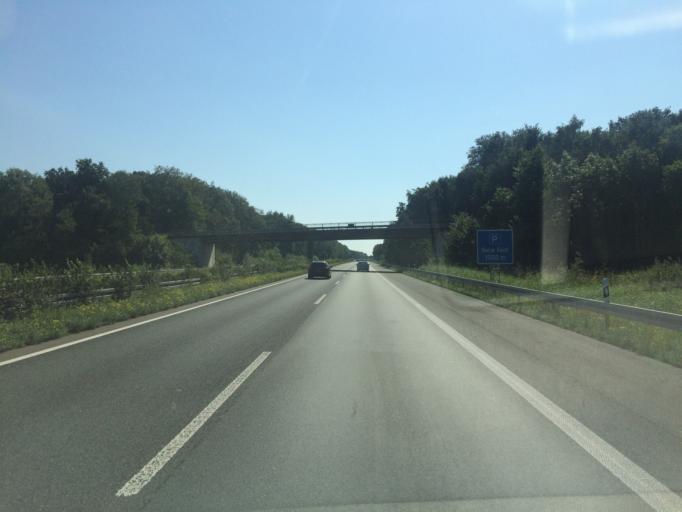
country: DE
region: North Rhine-Westphalia
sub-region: Regierungsbezirk Munster
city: Ascheberg
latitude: 51.8225
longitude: 7.6090
